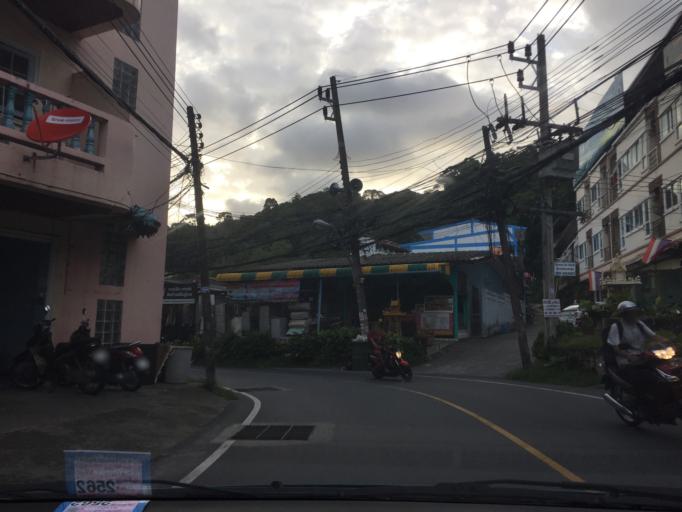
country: TH
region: Phuket
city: Patong
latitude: 7.8968
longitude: 98.3097
